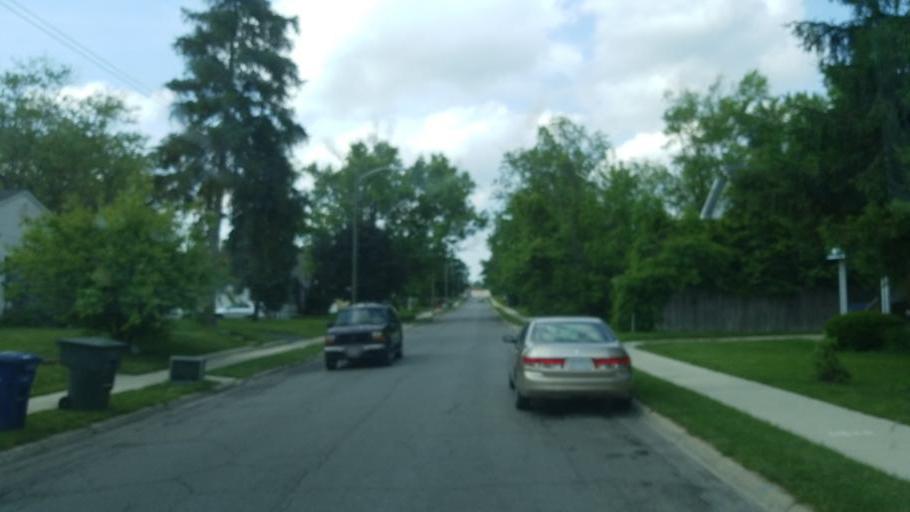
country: US
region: Ohio
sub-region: Franklin County
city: Minerva Park
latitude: 40.0236
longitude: -82.9598
